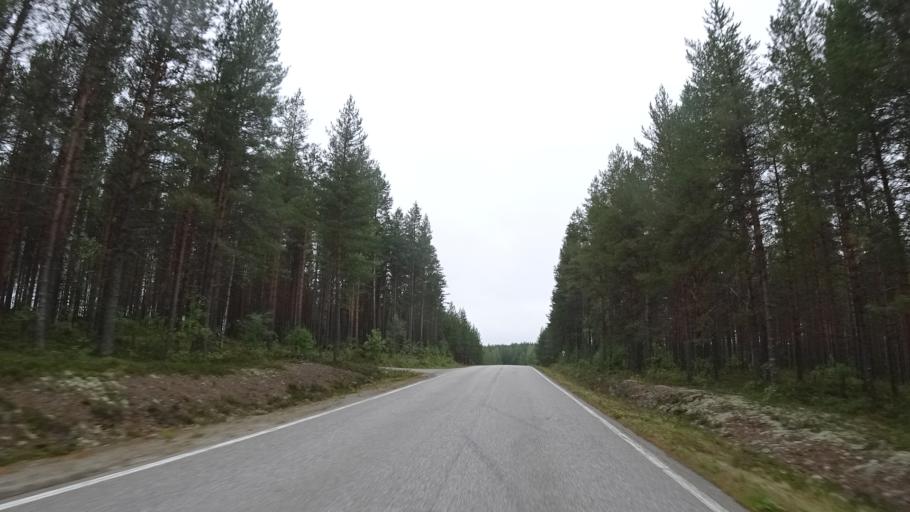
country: FI
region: North Karelia
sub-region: Pielisen Karjala
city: Lieksa
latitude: 63.3306
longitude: 30.2446
